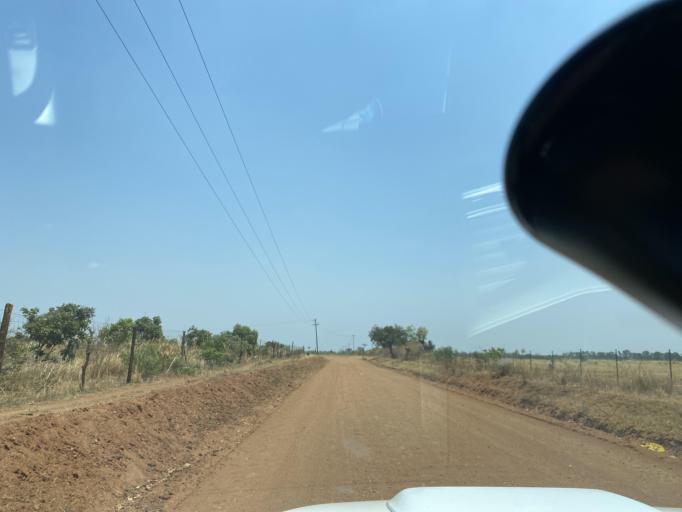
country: ZM
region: Lusaka
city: Lusaka
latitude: -15.4421
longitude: 28.0515
